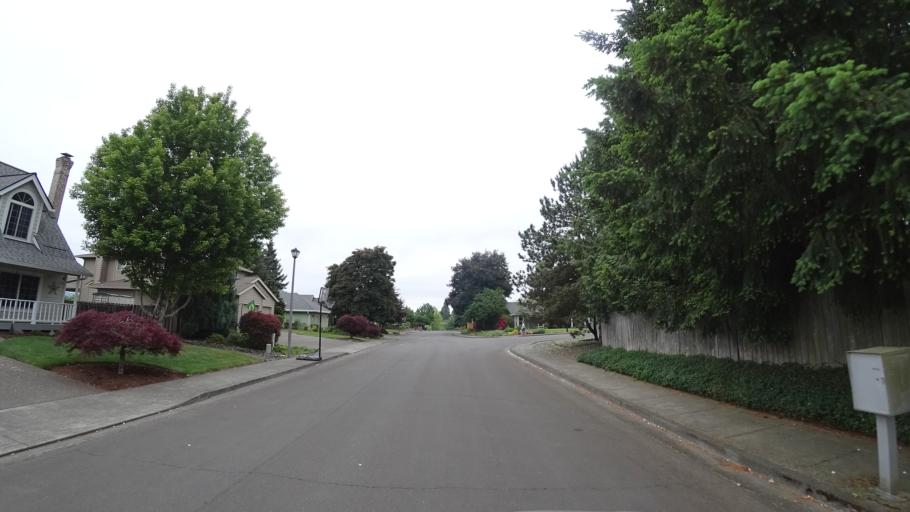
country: US
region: Oregon
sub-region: Washington County
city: Rockcreek
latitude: 45.5635
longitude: -122.8902
